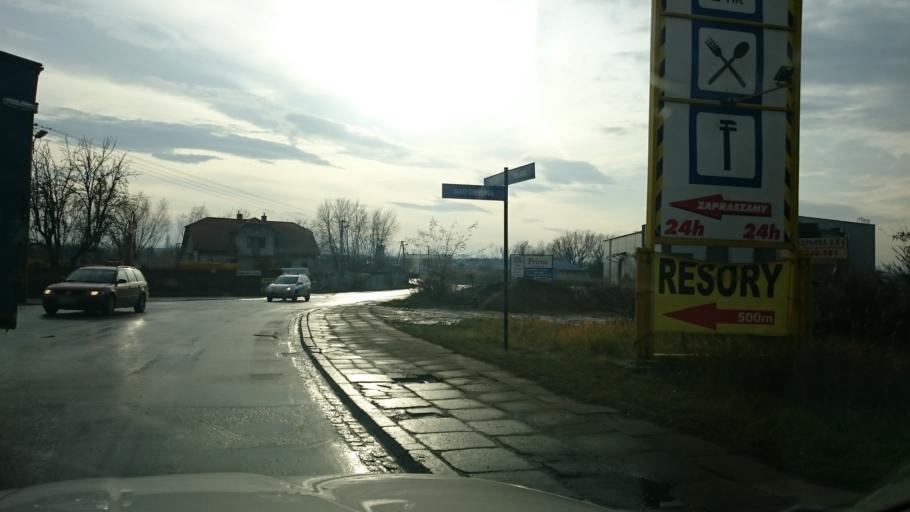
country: PL
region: Lesser Poland Voivodeship
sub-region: Powiat wielicki
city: Czarnochowice
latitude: 50.0335
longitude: 20.0421
